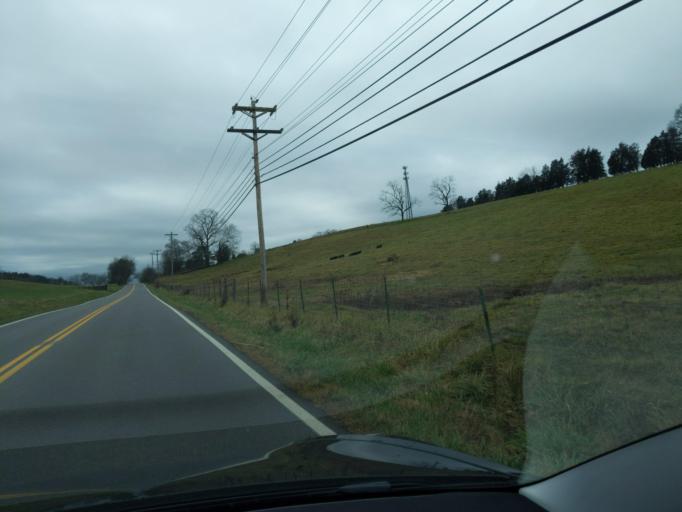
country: US
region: Tennessee
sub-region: Sevier County
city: Sevierville
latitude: 35.9697
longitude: -83.5606
